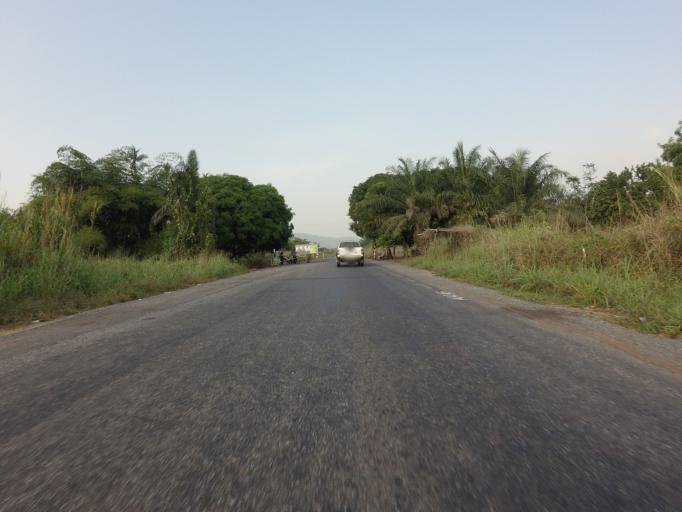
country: GH
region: Volta
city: Ho
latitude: 6.4627
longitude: 0.2208
